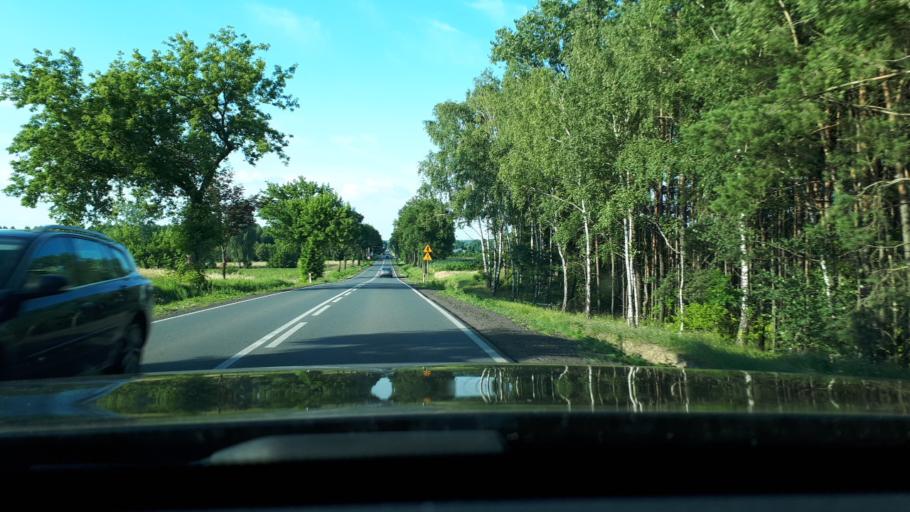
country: PL
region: Masovian Voivodeship
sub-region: Powiat ciechanowski
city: Ojrzen
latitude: 52.7429
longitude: 20.5254
